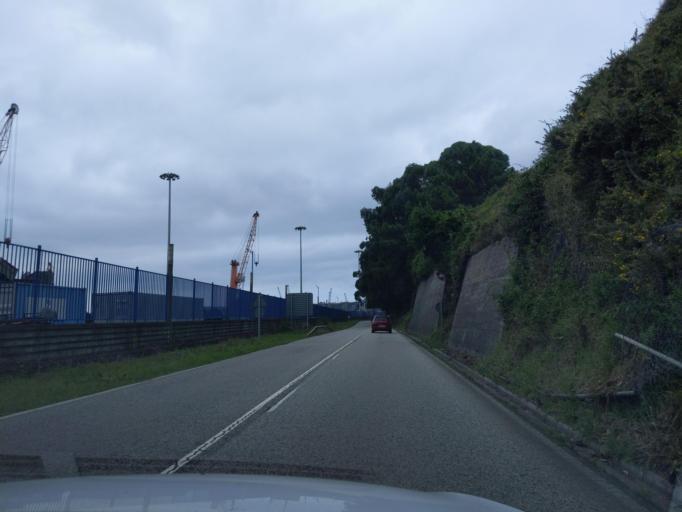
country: ES
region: Asturias
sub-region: Province of Asturias
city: Aviles
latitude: 43.5755
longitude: -5.9181
